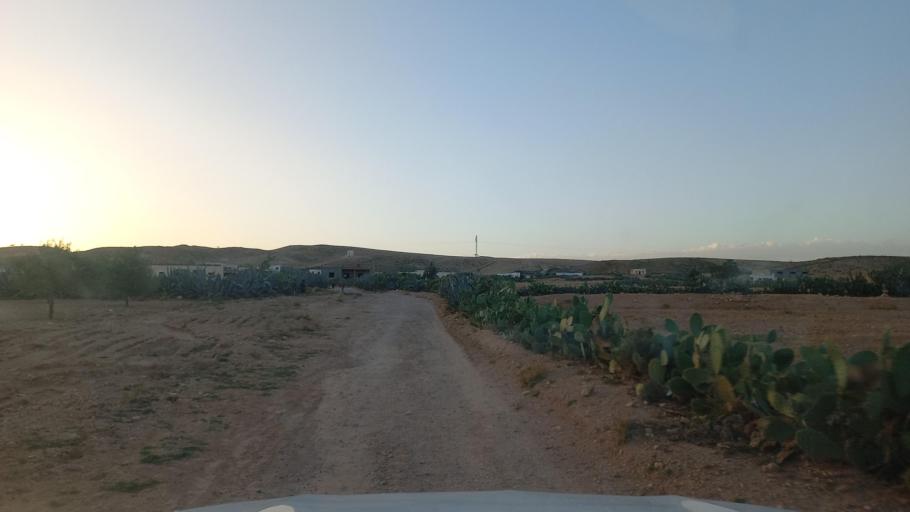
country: TN
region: Al Qasrayn
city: Sbiba
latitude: 35.3746
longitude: 9.0129
